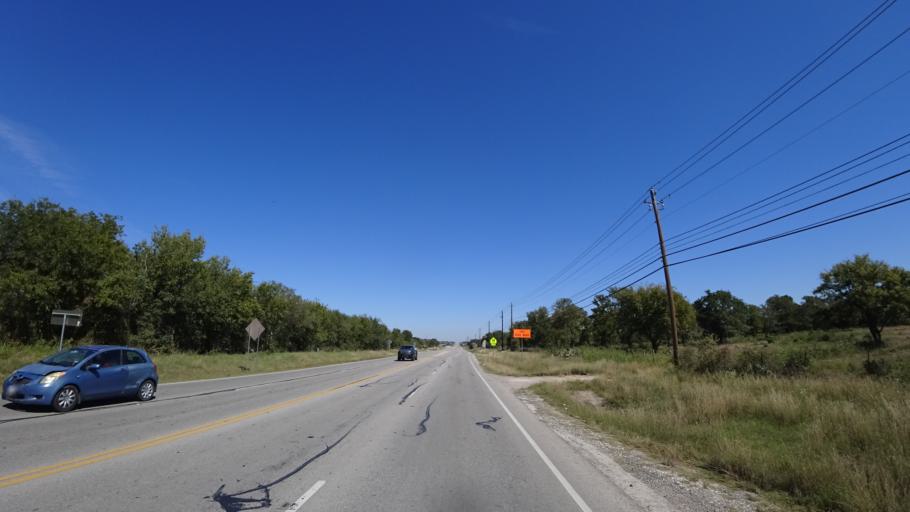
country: US
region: Texas
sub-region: Travis County
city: Hornsby Bend
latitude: 30.2779
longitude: -97.6365
